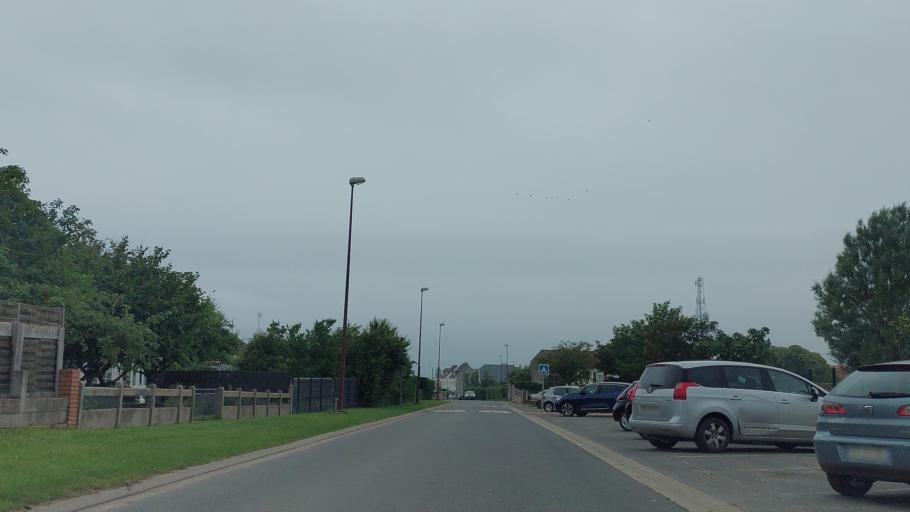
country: FR
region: Picardie
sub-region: Departement de la Somme
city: Ault
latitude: 50.1006
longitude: 1.4569
